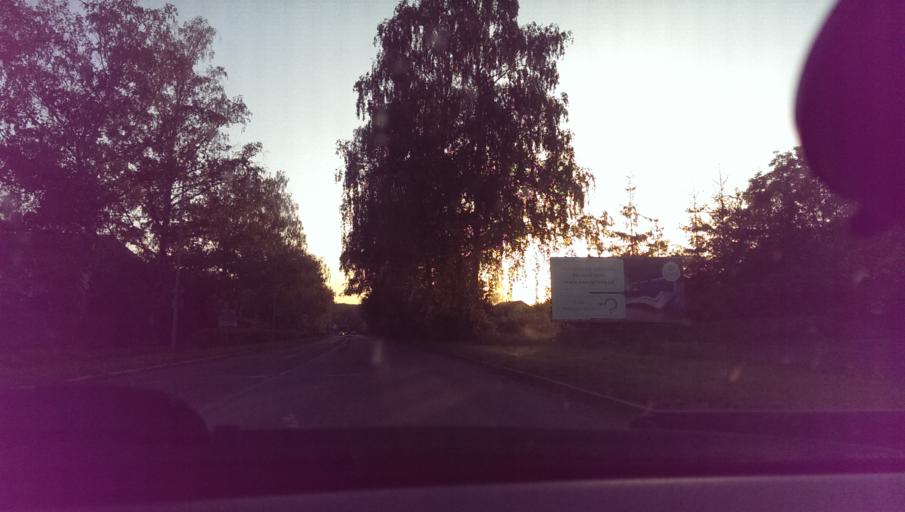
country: CZ
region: Zlin
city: Valasske Mezirici
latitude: 49.4774
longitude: 17.9781
